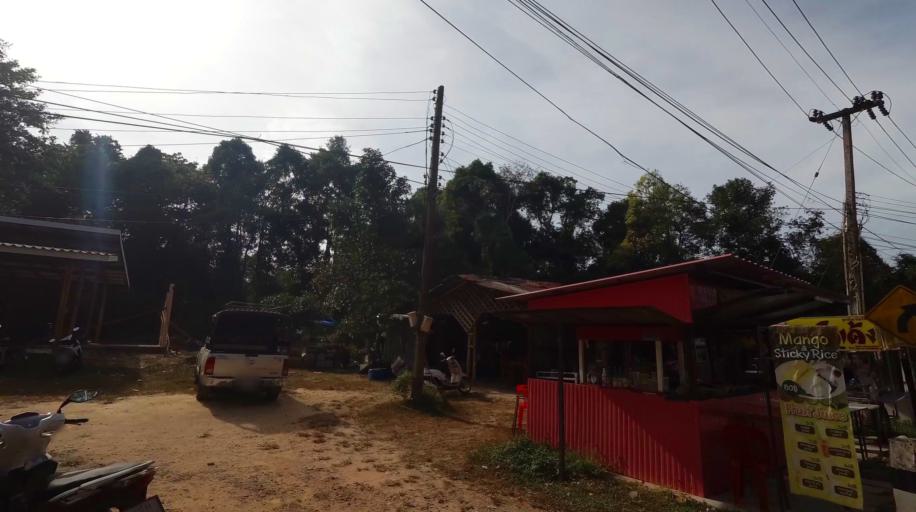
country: TH
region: Trat
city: Ko Kut
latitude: 11.6088
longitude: 102.5421
